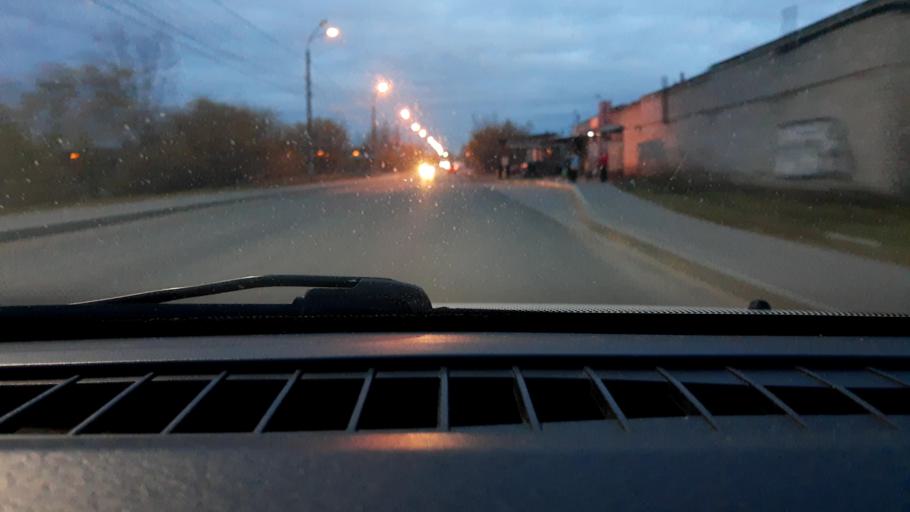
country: RU
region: Nizjnij Novgorod
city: Gorbatovka
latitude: 56.3601
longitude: 43.7967
